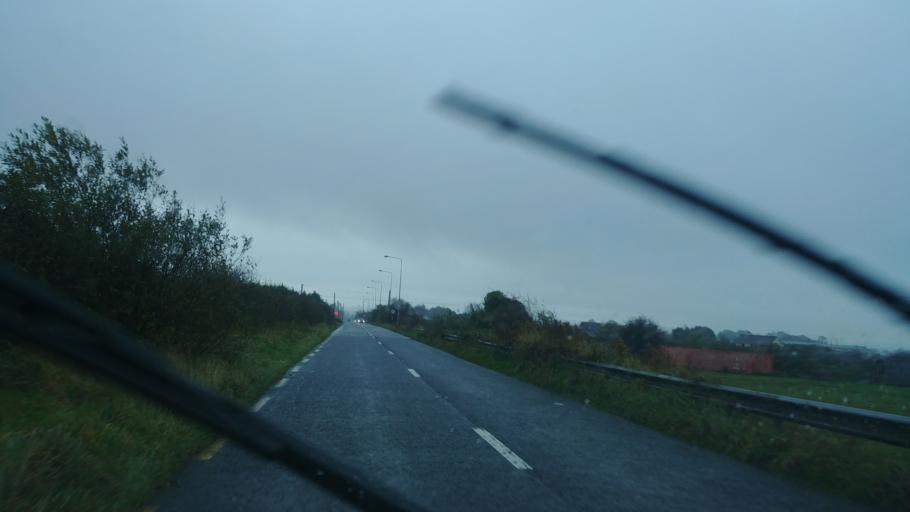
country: IE
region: Connaught
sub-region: Roscommon
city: Ballaghaderreen
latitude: 53.9087
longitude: -8.5935
